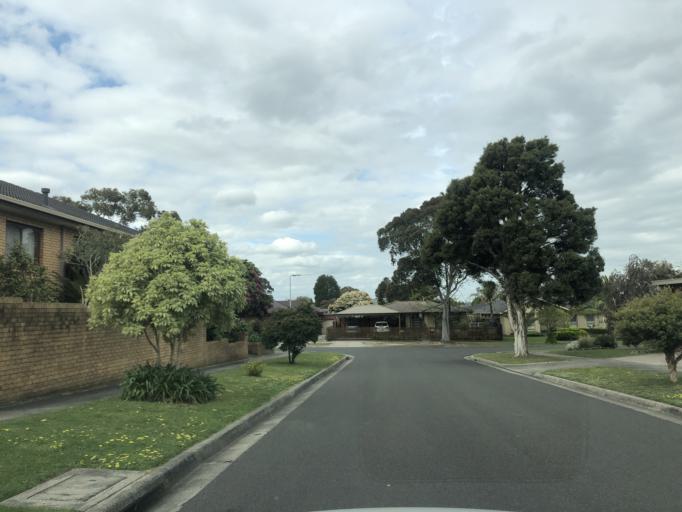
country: AU
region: Victoria
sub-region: Greater Dandenong
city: Noble Park North
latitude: -37.9342
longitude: 145.1954
